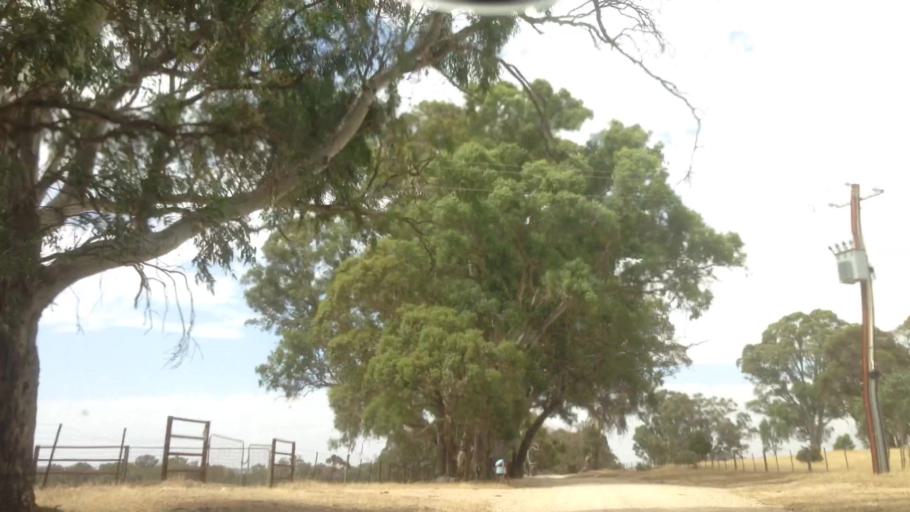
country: AU
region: South Australia
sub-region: Barossa
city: Williamstown
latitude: -34.6966
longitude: 138.9908
